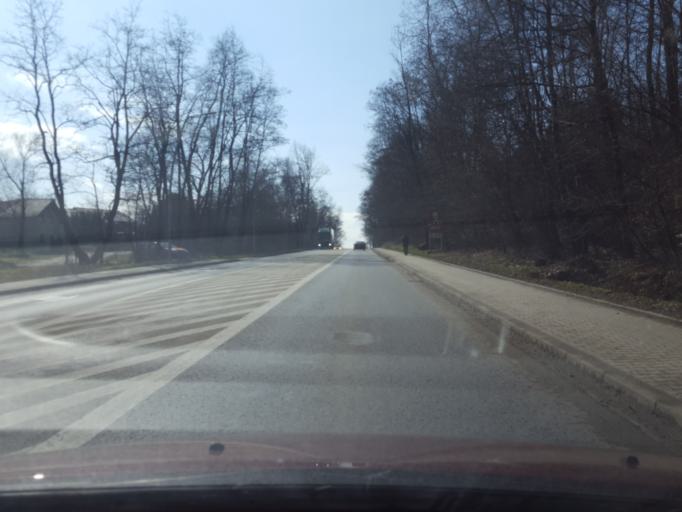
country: PL
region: Lesser Poland Voivodeship
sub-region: Powiat nowosadecki
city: Nowy Sacz
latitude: 49.6457
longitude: 20.6907
